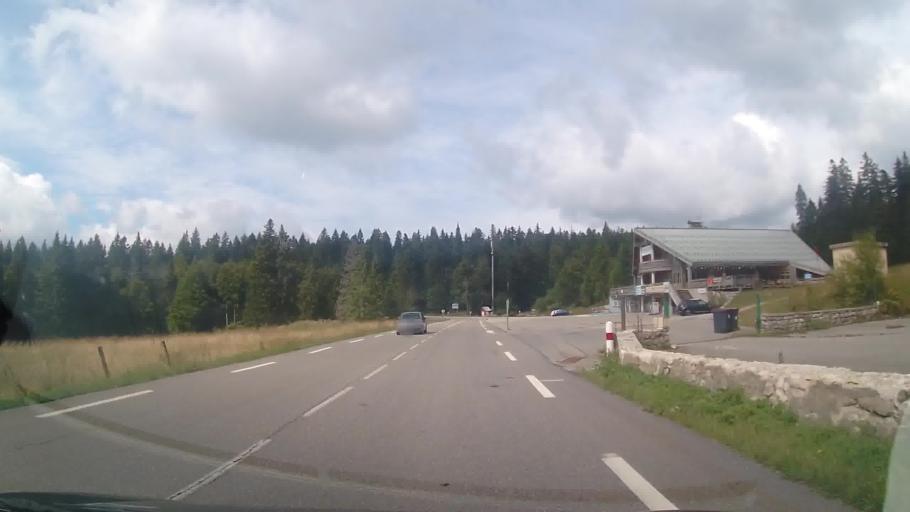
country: FR
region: Rhone-Alpes
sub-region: Departement de l'Ain
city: Gex
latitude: 46.3883
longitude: 6.0533
